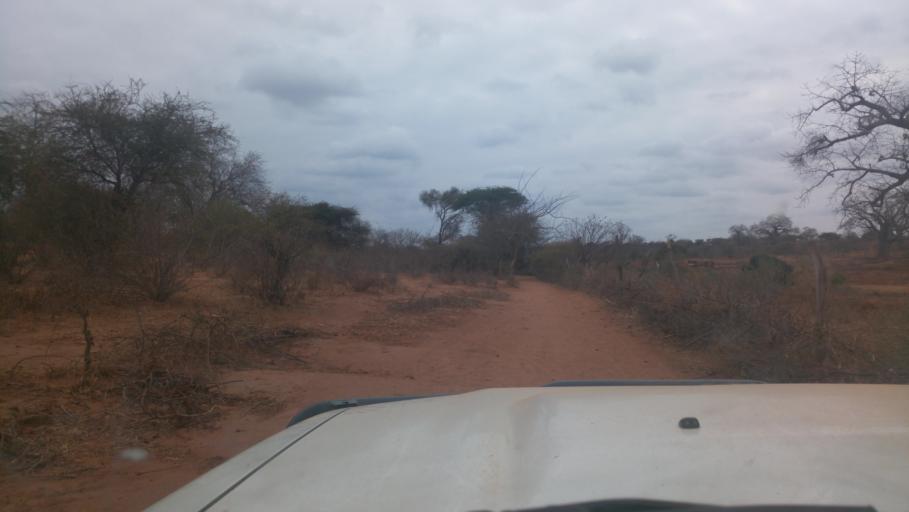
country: KE
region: Makueni
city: Makueni
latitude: -1.9689
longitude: 38.0789
